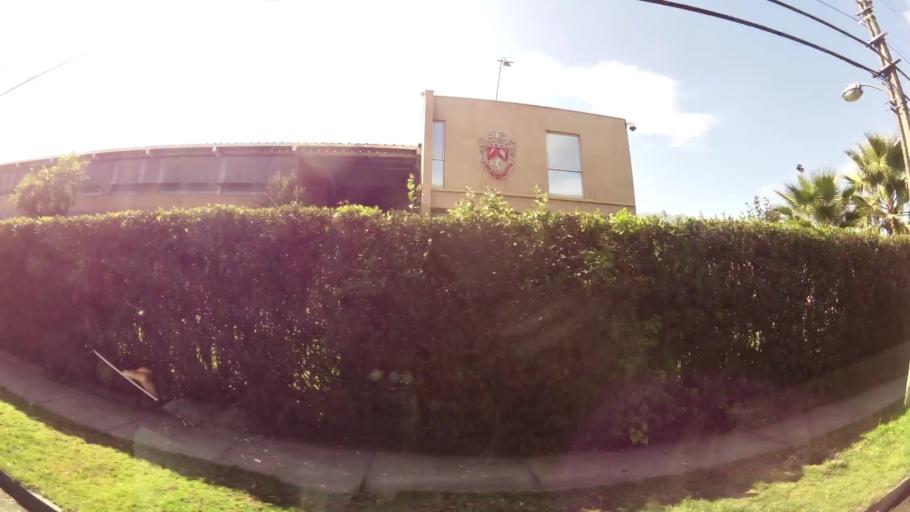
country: CL
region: Santiago Metropolitan
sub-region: Provincia de Santiago
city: Villa Presidente Frei, Nunoa, Santiago, Chile
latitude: -33.4513
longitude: -70.5281
